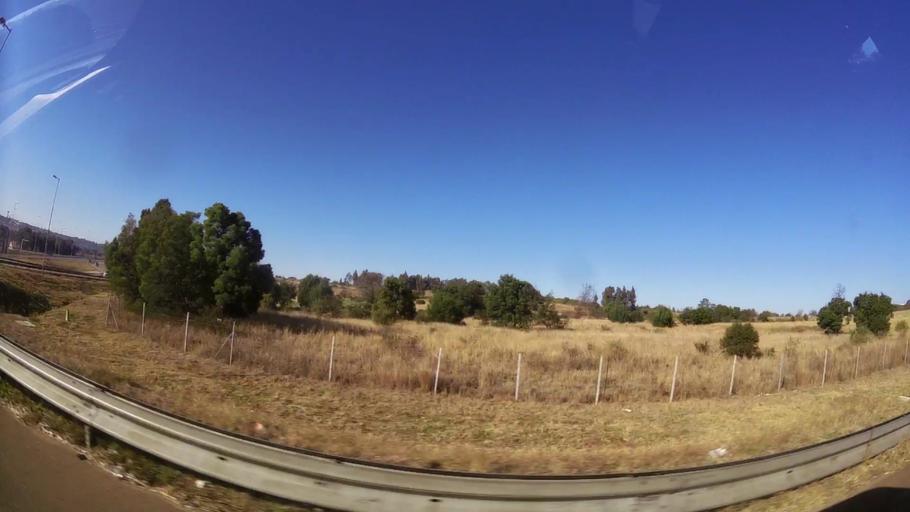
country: ZA
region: Gauteng
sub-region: City of Tshwane Metropolitan Municipality
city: Centurion
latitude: -25.8144
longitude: 28.2331
